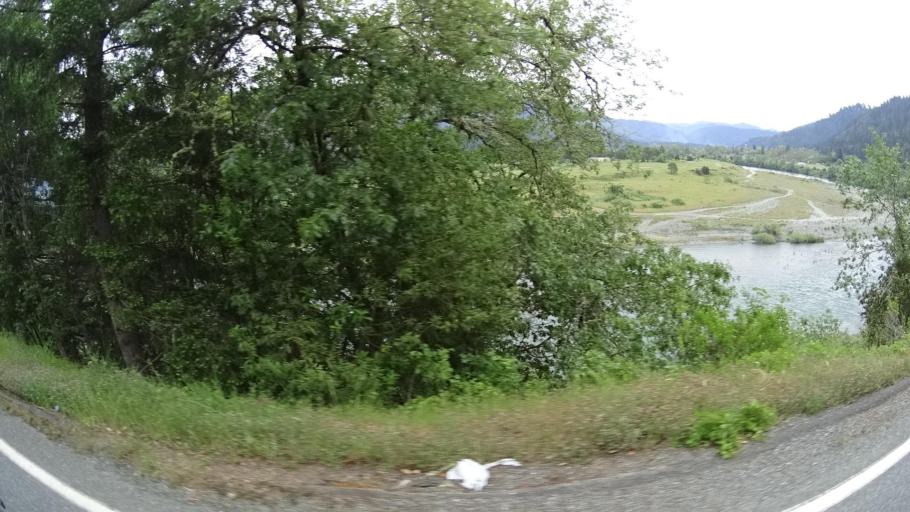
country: US
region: California
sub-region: Humboldt County
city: Willow Creek
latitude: 41.0675
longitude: -123.6946
